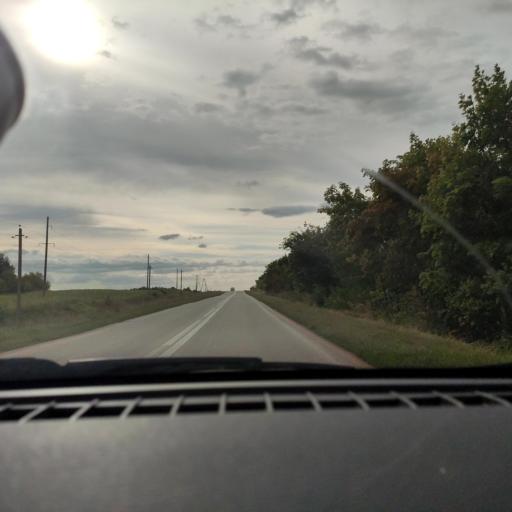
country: RU
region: Samara
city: Georgiyevka
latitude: 53.4286
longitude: 50.7918
